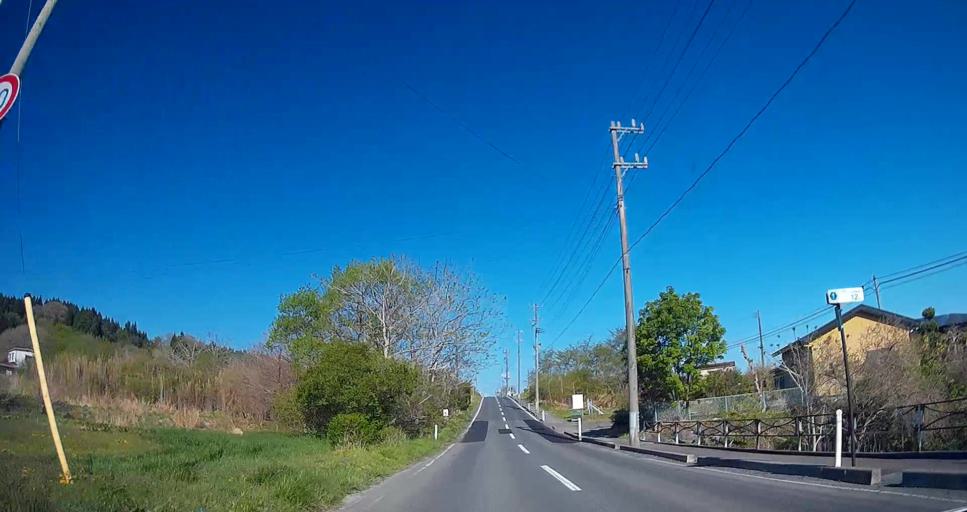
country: JP
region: Aomori
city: Hachinohe
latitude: 40.5148
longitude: 141.5952
